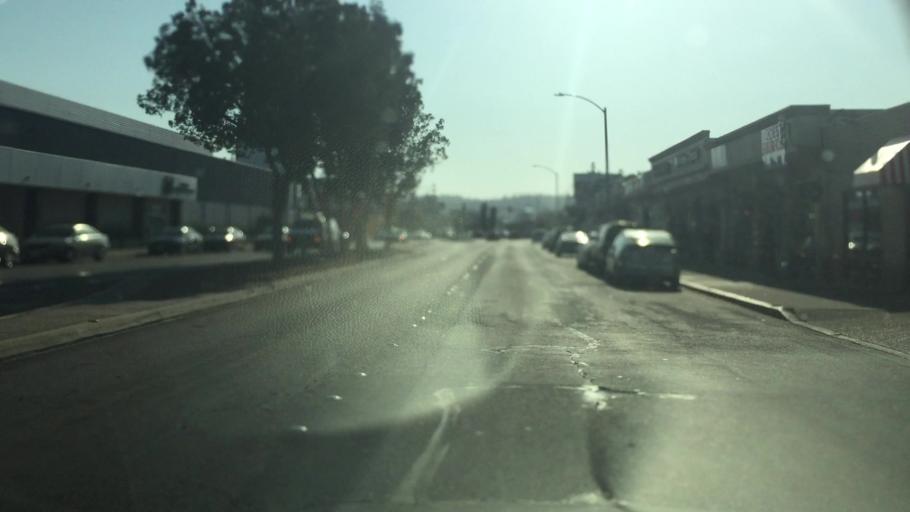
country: US
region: California
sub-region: San Diego County
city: El Cajon
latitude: 32.7950
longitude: -116.9554
